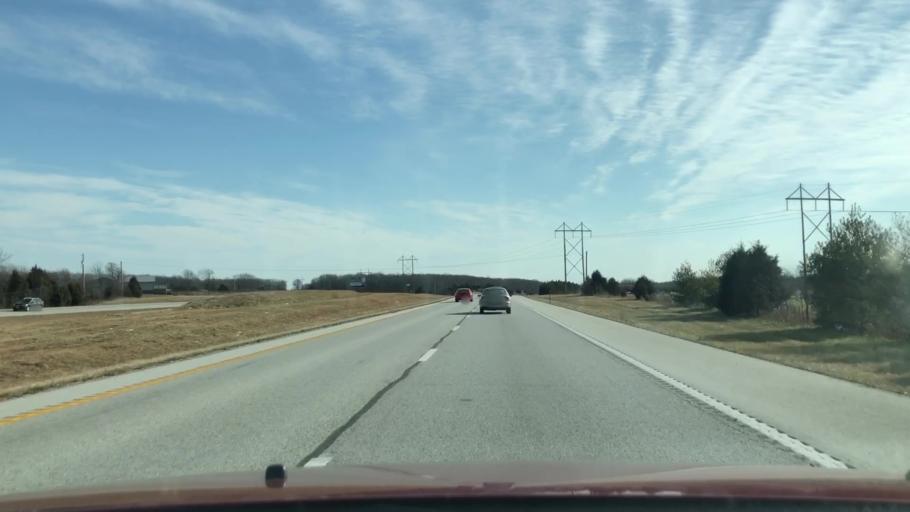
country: US
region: Missouri
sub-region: Webster County
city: Seymour
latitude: 37.1177
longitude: -92.6827
